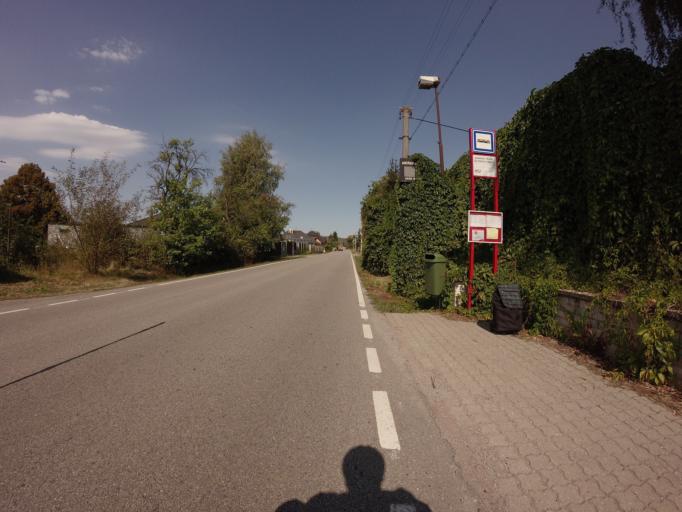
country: CZ
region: Central Bohemia
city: Kamenny Privoz
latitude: 49.8600
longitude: 14.5145
